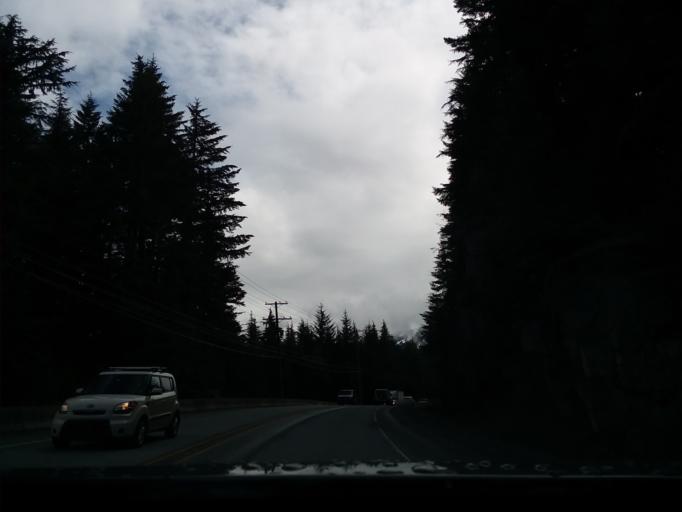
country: CA
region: British Columbia
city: Whistler
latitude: 50.1039
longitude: -122.9857
